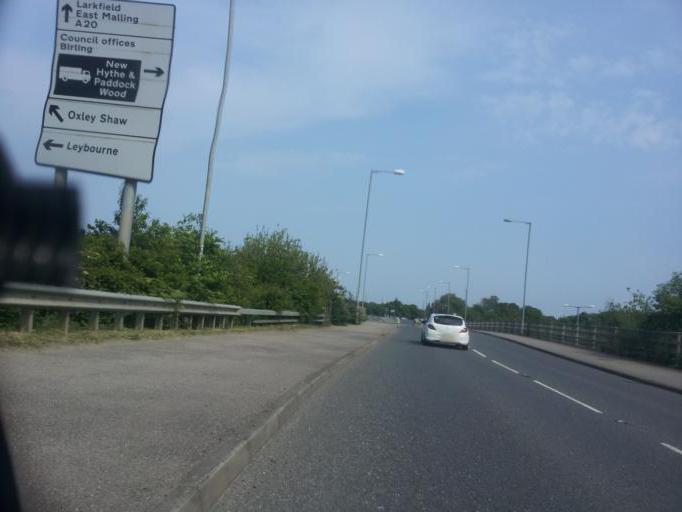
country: GB
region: England
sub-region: Kent
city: West Malling
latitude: 51.2988
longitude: 0.4164
